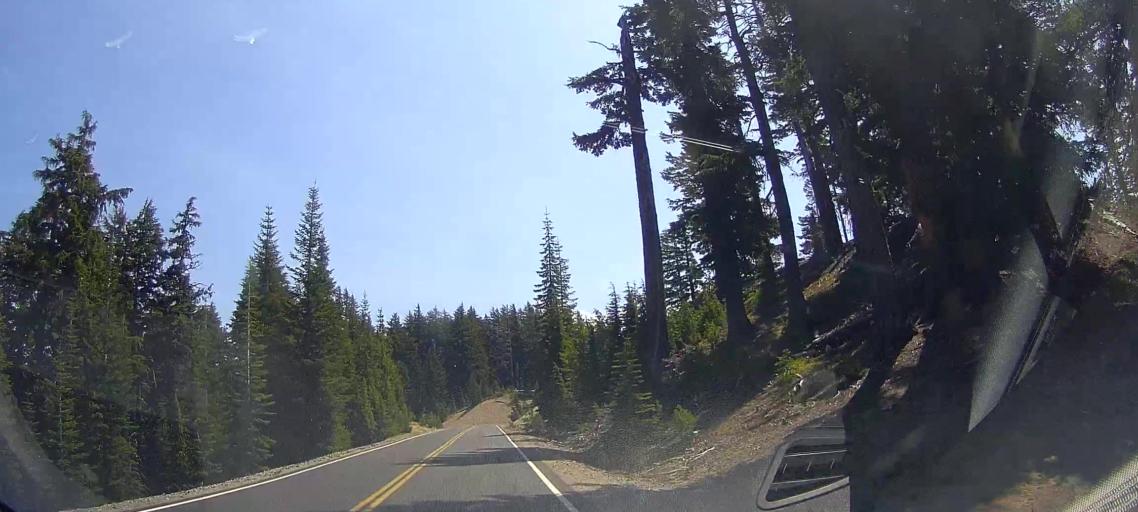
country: US
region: Oregon
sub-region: Jackson County
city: Shady Cove
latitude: 42.9801
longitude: -122.1139
